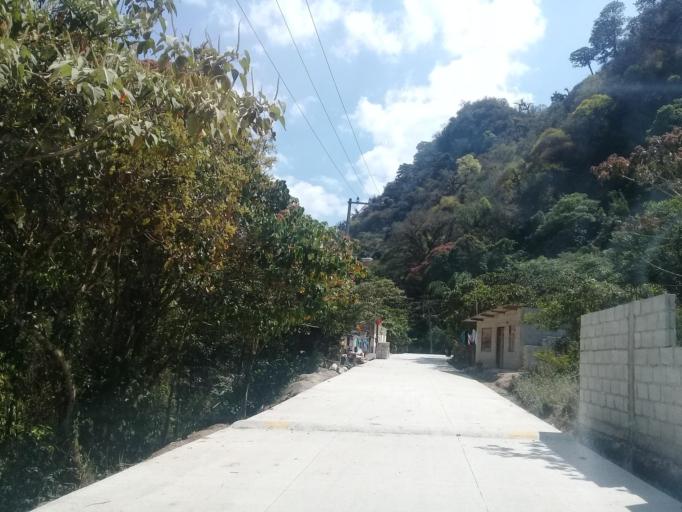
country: MX
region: Veracruz
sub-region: Tlilapan
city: Tonalixco
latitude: 18.8080
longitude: -97.0647
